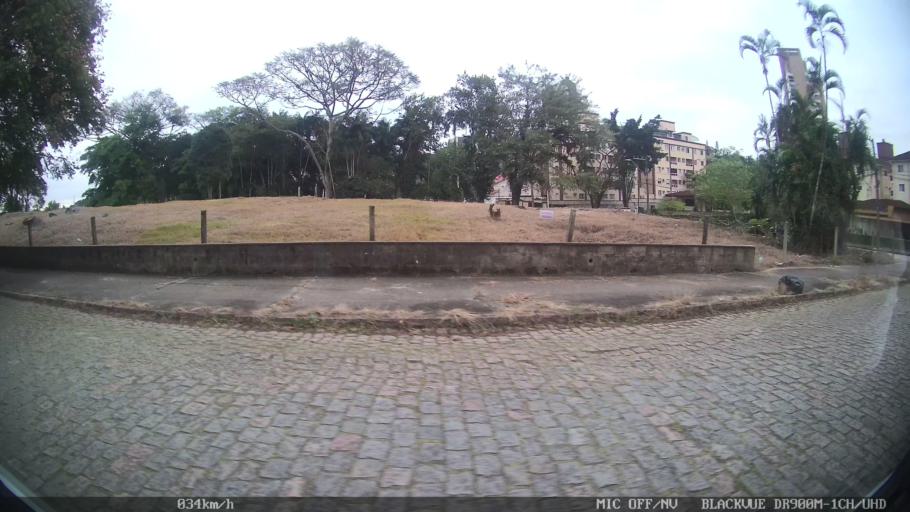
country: BR
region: Santa Catarina
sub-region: Joinville
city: Joinville
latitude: -26.3088
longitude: -48.8590
